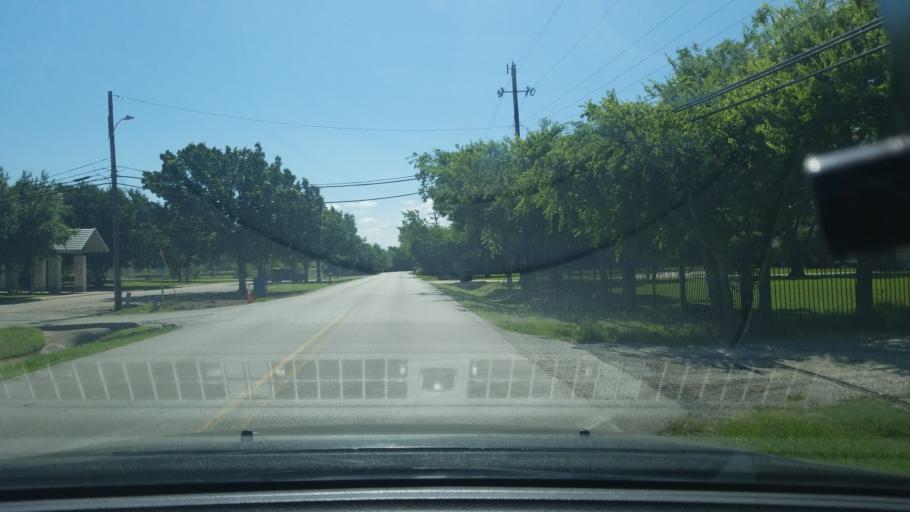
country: US
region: Texas
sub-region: Dallas County
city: Sunnyvale
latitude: 32.7945
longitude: -96.5586
